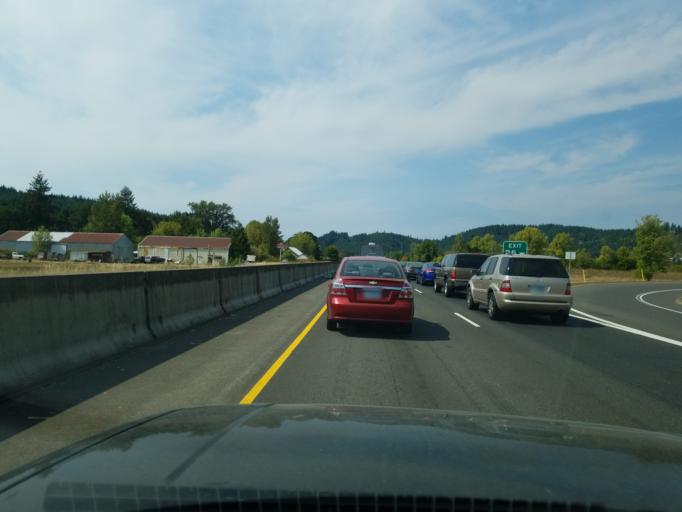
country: US
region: Oregon
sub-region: Yamhill County
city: Willamina
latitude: 45.0552
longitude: -123.5430
